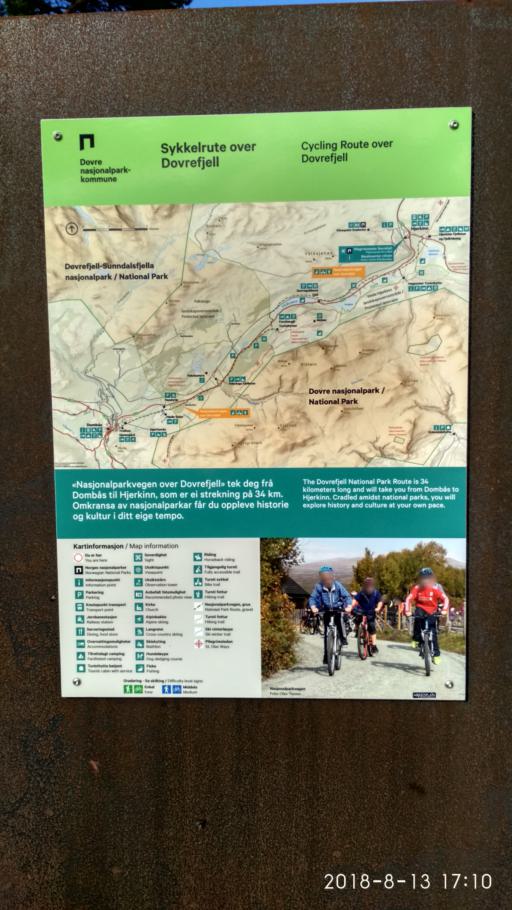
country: NO
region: Oppland
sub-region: Dovre
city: Dombas
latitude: 62.0771
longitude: 9.1452
